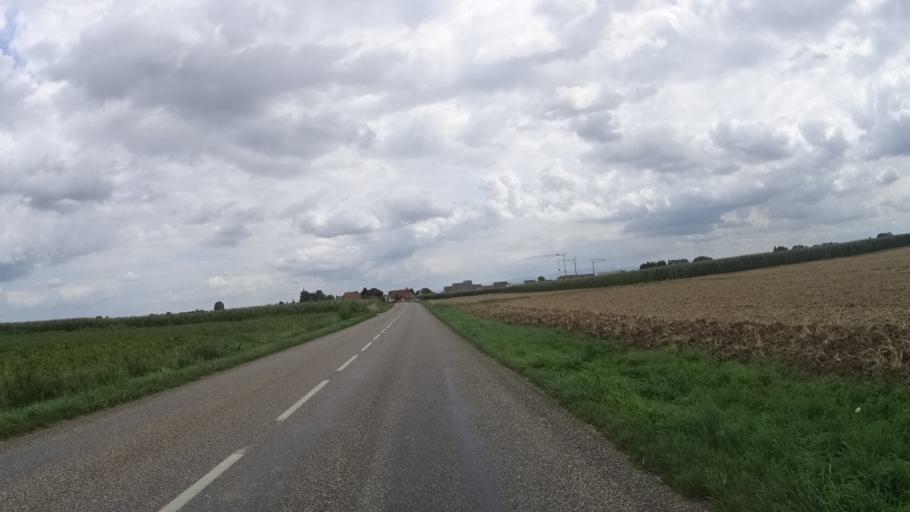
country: FR
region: Alsace
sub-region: Departement du Bas-Rhin
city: Weyersheim
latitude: 48.7173
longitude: 7.7888
